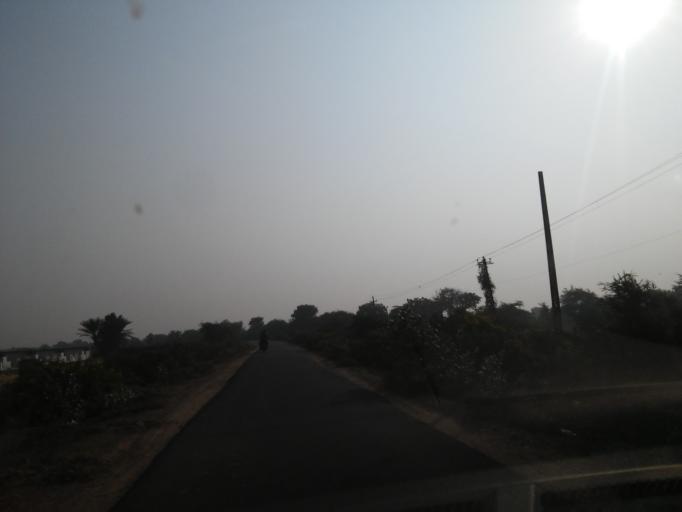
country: IN
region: Gujarat
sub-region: Kachchh
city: Mandvi
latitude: 22.8317
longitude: 69.4118
